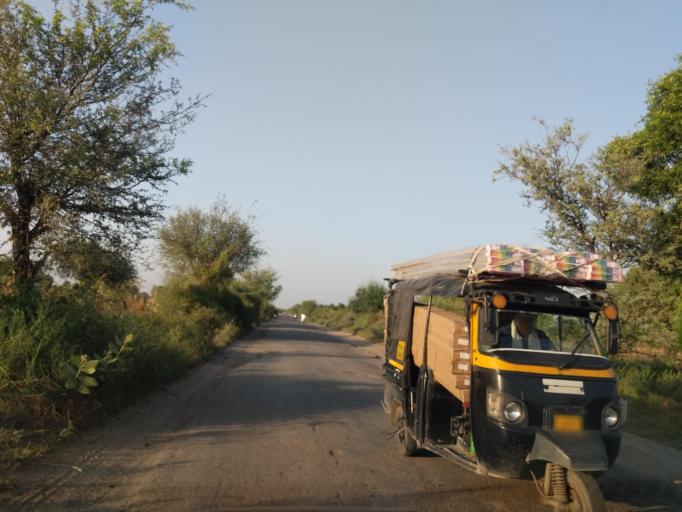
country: IN
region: Rajasthan
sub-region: Churu
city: Rajgarh
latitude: 28.5688
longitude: 75.3681
